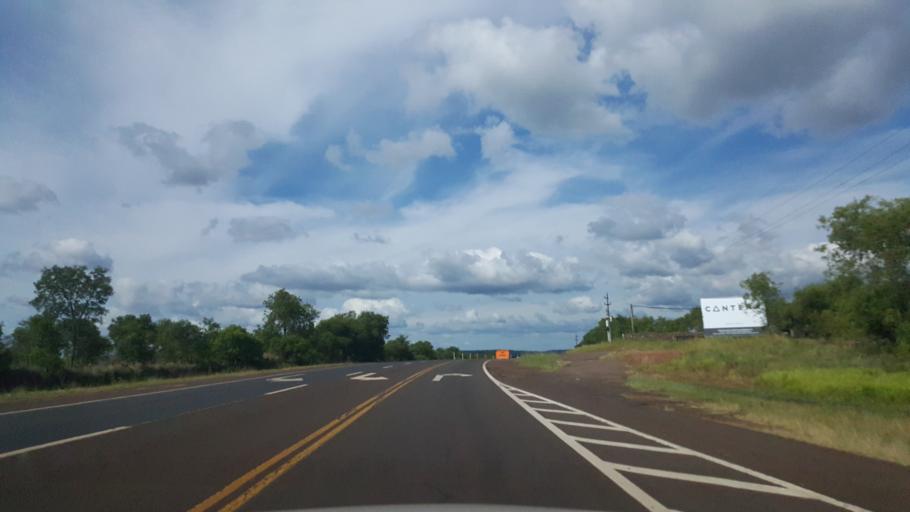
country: AR
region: Misiones
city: Santa Ana
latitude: -27.4124
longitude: -55.6103
